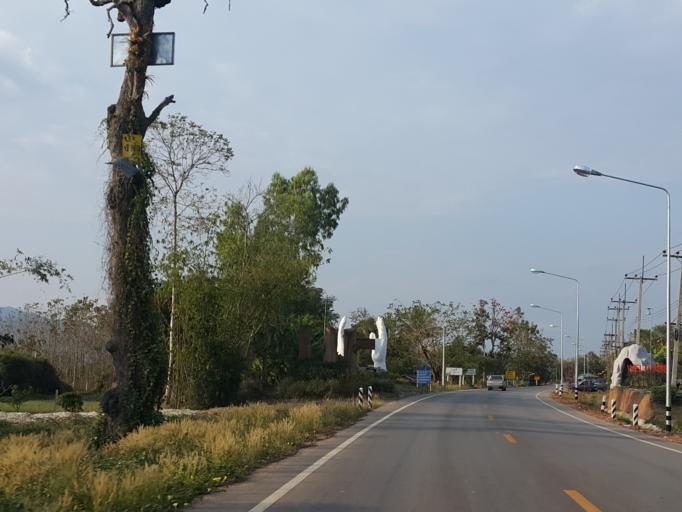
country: TH
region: Lampang
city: Chae Hom
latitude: 18.5275
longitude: 99.4777
